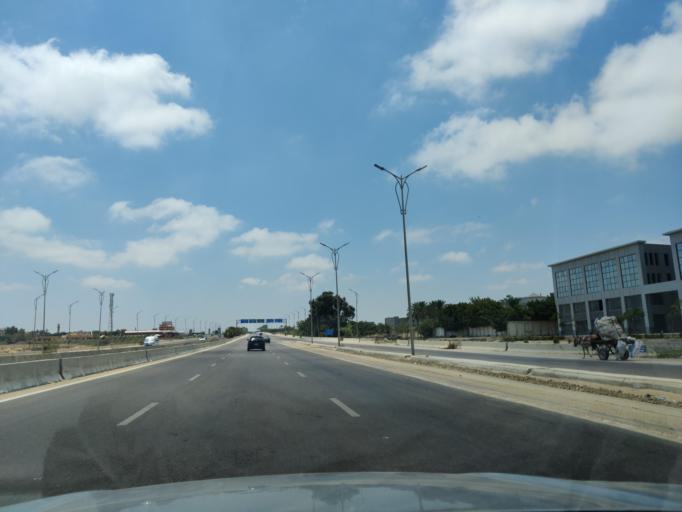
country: EG
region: Alexandria
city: Alexandria
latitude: 30.9820
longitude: 29.6594
